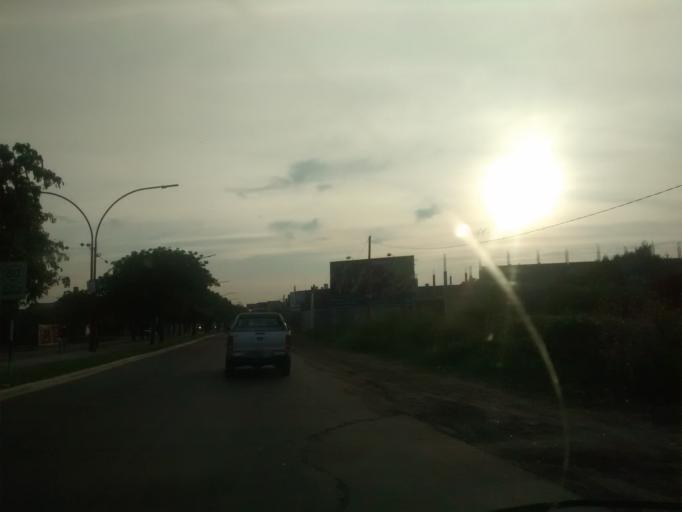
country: AR
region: Chaco
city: Resistencia
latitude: -27.4345
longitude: -58.9681
